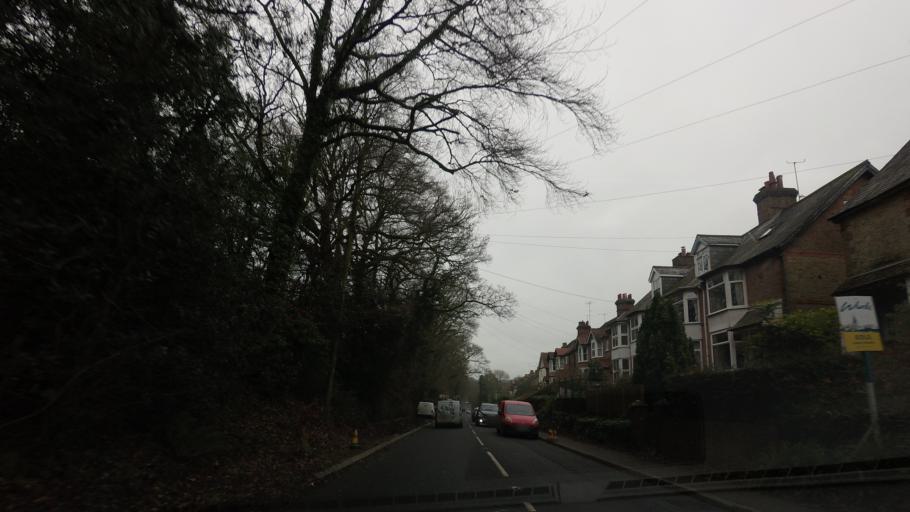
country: GB
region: England
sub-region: Kent
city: Hawkhurst
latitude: 51.0528
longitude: 0.5081
